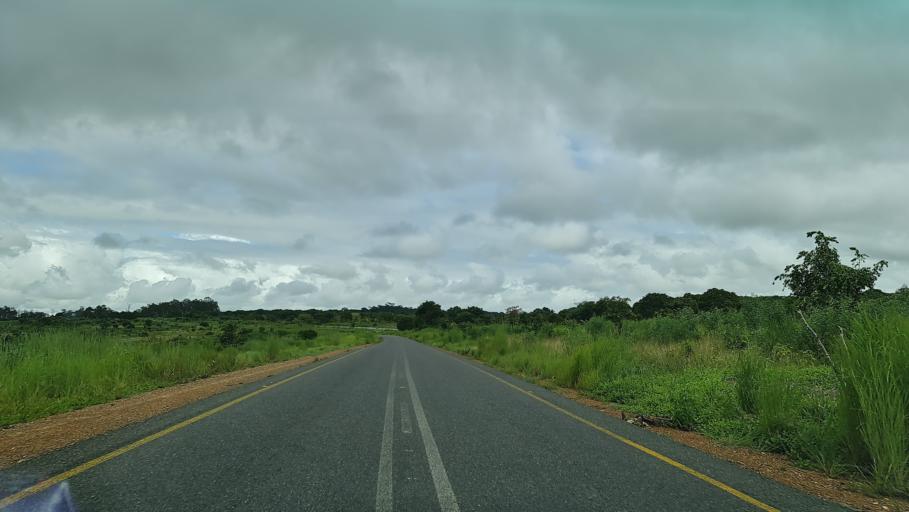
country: MZ
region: Nampula
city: Nampula
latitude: -14.9780
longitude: 38.5312
